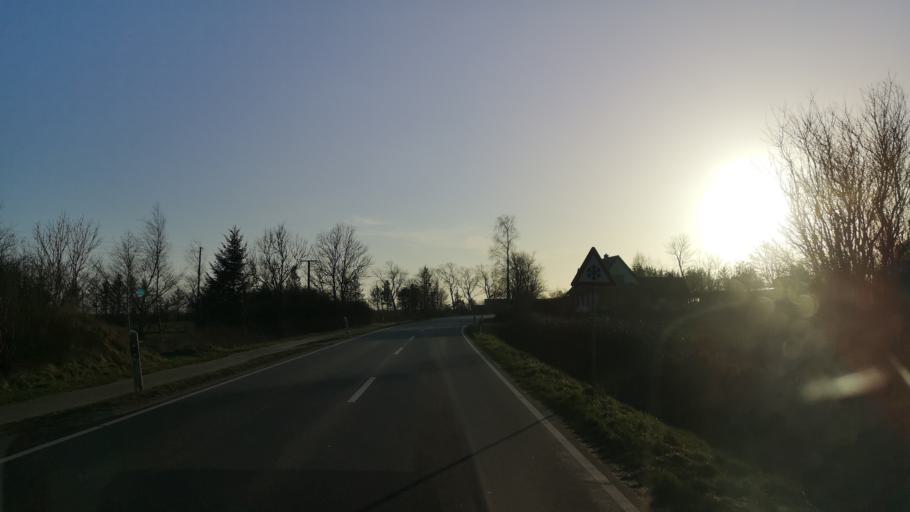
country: DE
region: Schleswig-Holstein
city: Grosssolt
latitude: 54.6825
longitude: 9.4916
